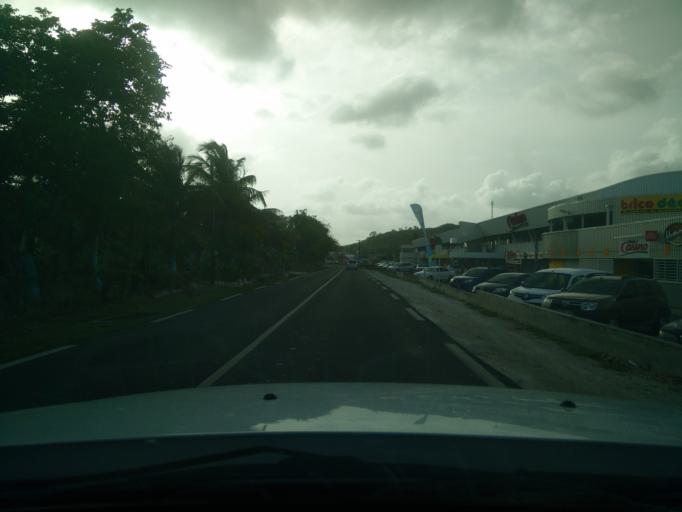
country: GP
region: Guadeloupe
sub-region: Guadeloupe
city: Saint-Francois
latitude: 16.2588
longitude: -61.2909
